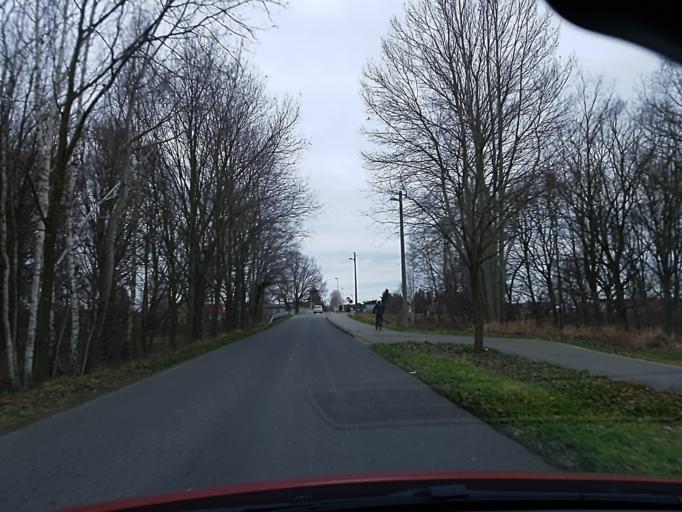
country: DE
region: Brandenburg
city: Elsterwerda
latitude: 51.4539
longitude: 13.5083
